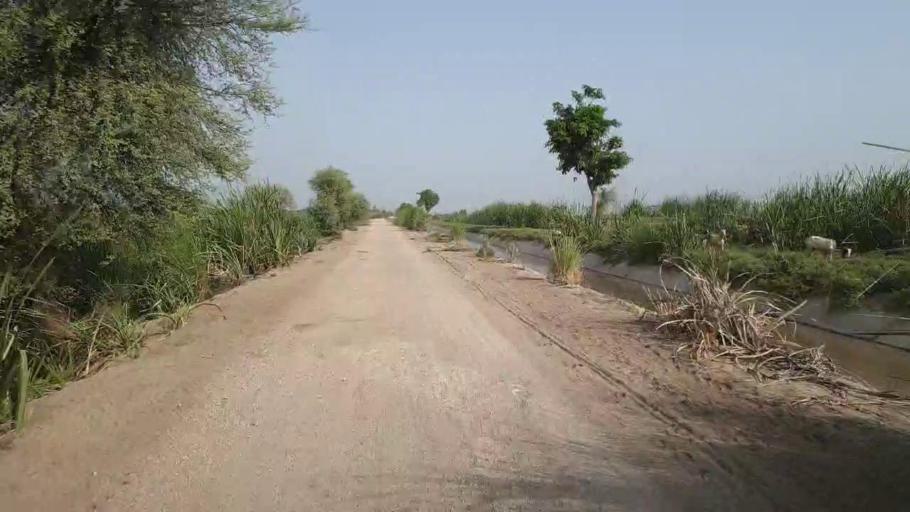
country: PK
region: Sindh
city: Daur
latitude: 26.3342
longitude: 68.1875
